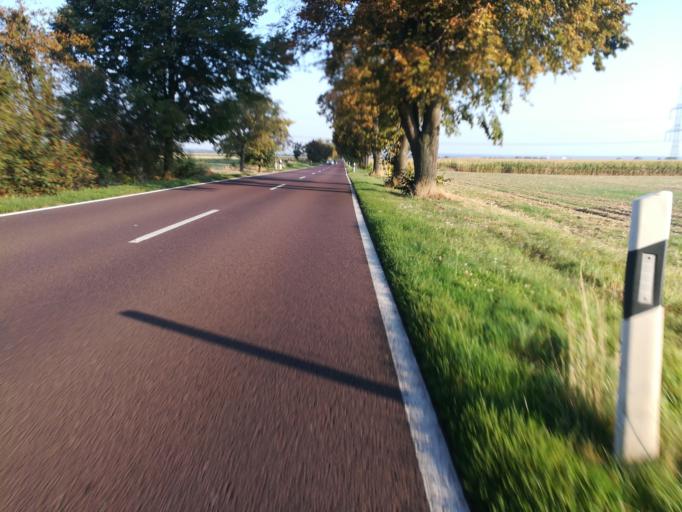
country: DE
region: Saxony-Anhalt
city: Gross Santersleben
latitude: 52.2419
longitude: 11.4391
